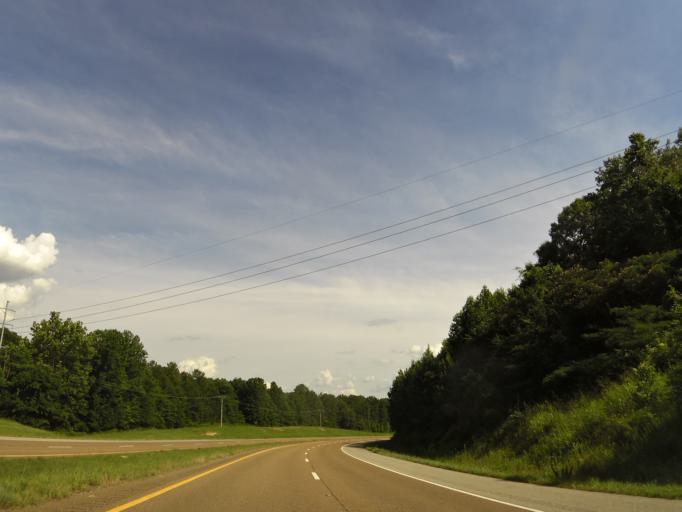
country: US
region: Tennessee
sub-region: Carroll County
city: Huntingdon
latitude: 36.0203
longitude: -88.3959
